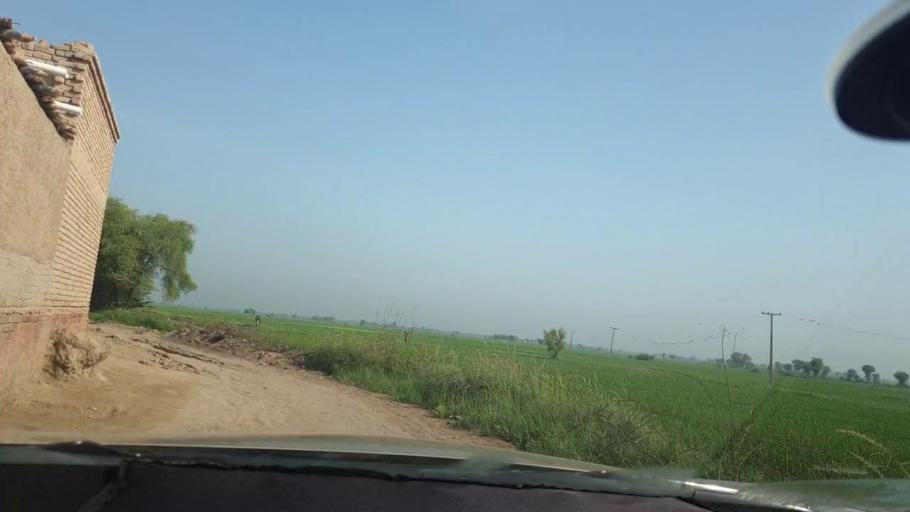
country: PK
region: Sindh
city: Kambar
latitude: 27.6682
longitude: 68.0119
